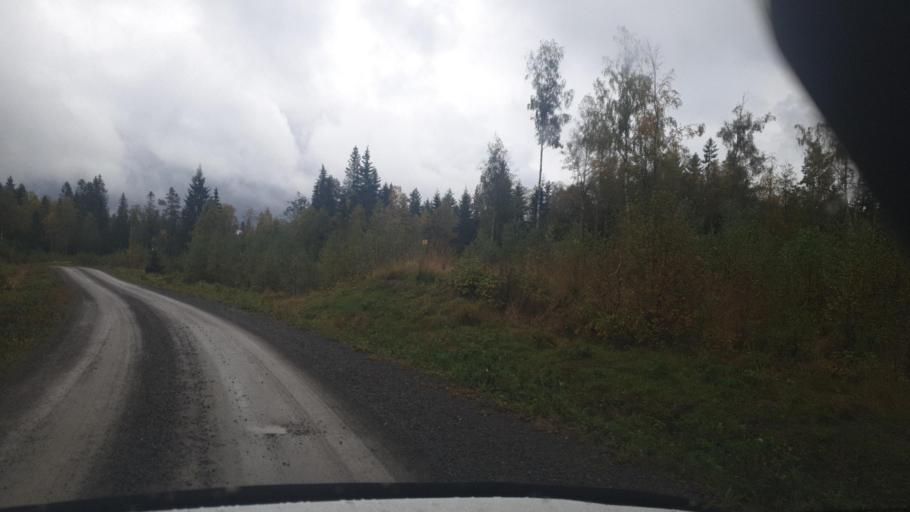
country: SE
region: Vaermland
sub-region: Arvika Kommun
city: Arvika
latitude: 59.8623
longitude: 12.8260
